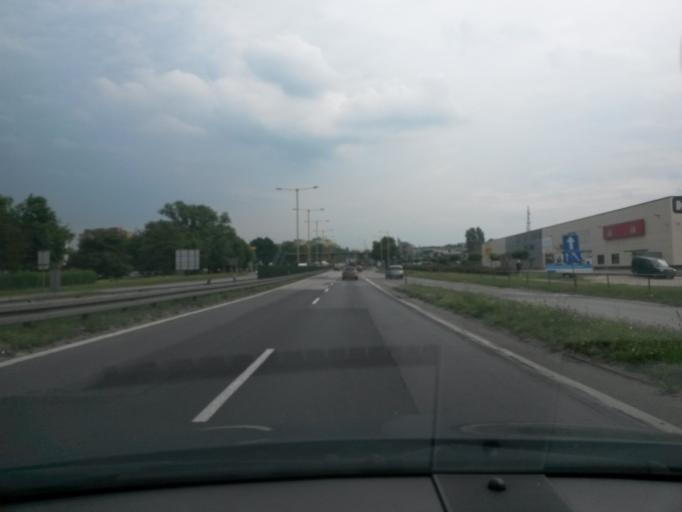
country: PL
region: Silesian Voivodeship
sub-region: Czestochowa
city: Czestochowa
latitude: 50.7824
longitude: 19.1443
